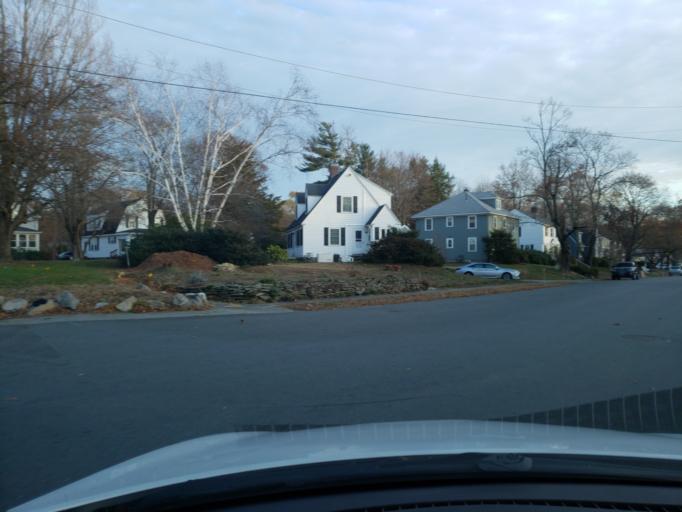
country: US
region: Massachusetts
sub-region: Essex County
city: Andover
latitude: 42.6590
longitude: -71.1307
